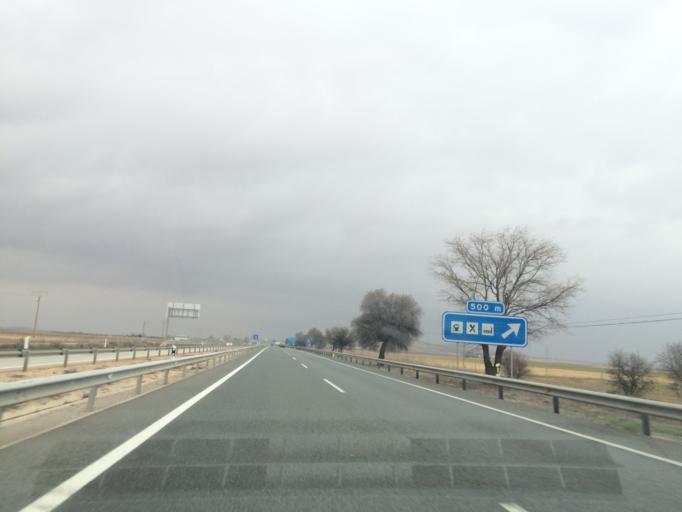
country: ES
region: Castille-La Mancha
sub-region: Province of Toledo
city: Madridejos
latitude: 39.5033
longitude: -3.5267
